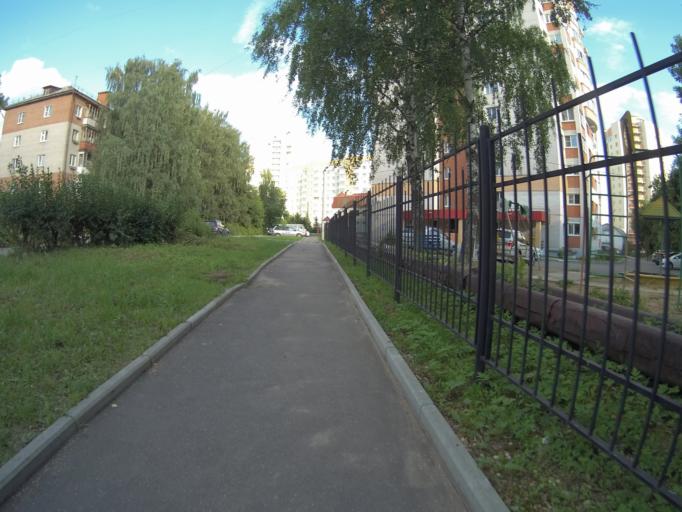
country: RU
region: Vladimir
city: Vladimir
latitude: 56.1401
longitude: 40.3861
